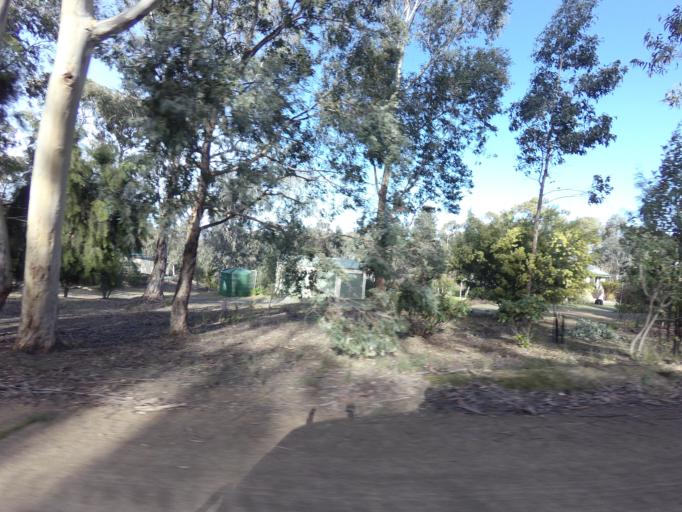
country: AU
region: Tasmania
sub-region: Kingborough
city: Kettering
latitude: -43.1183
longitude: 147.2669
